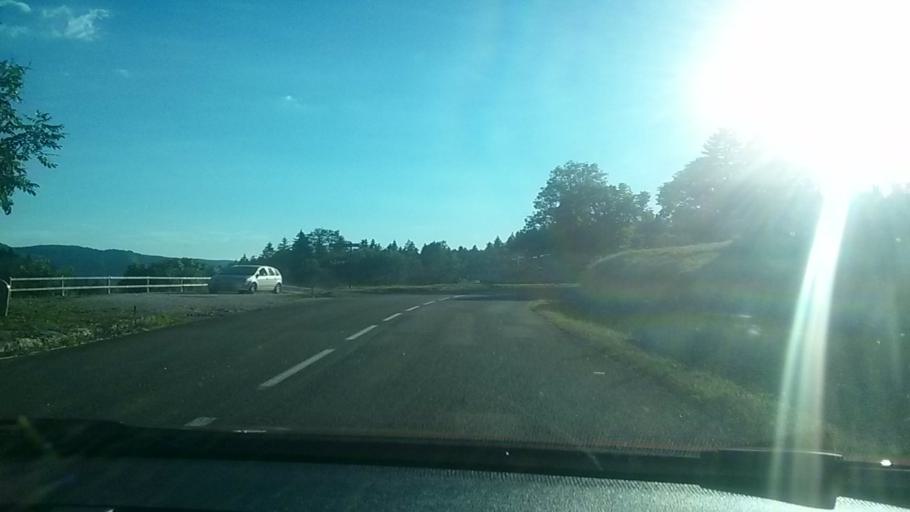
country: FR
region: Franche-Comte
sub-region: Departement du Jura
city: Saint-Claude
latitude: 46.3851
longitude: 5.9361
